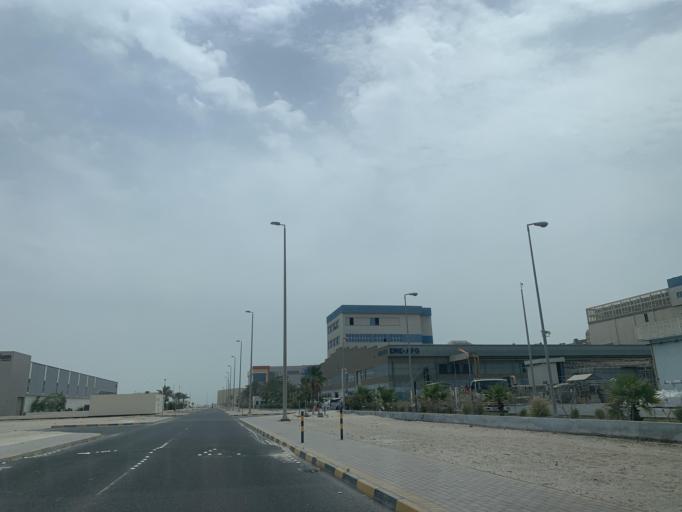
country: BH
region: Muharraq
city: Al Hadd
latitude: 26.2181
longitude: 50.6761
